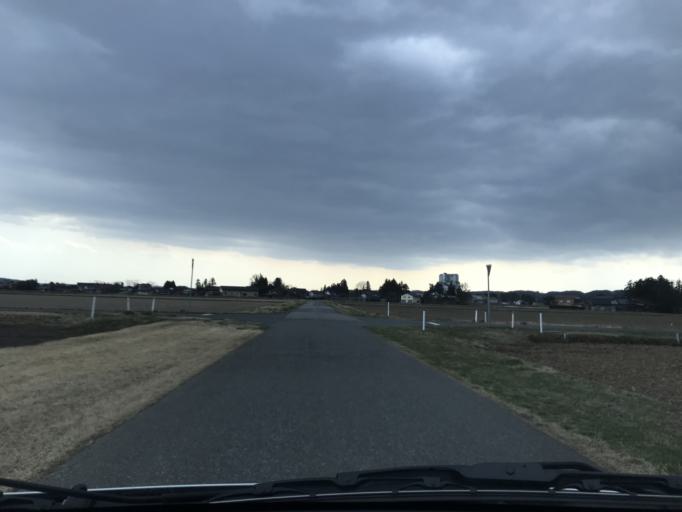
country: JP
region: Iwate
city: Mizusawa
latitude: 39.0727
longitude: 141.1540
